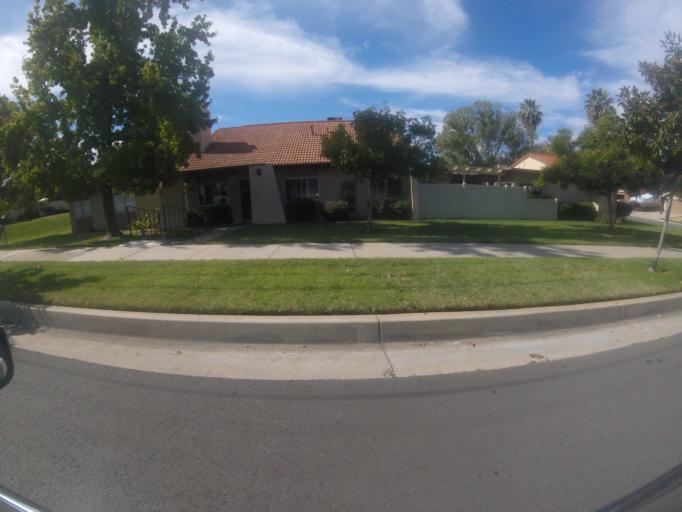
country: US
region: California
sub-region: San Bernardino County
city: Mentone
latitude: 34.0571
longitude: -117.1477
